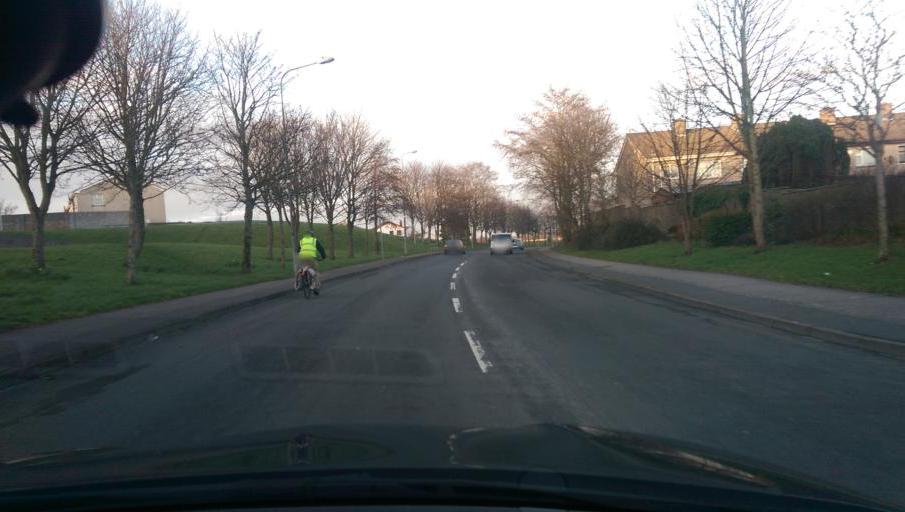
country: IE
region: Connaught
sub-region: County Galway
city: Gaillimh
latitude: 53.2802
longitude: -9.0770
